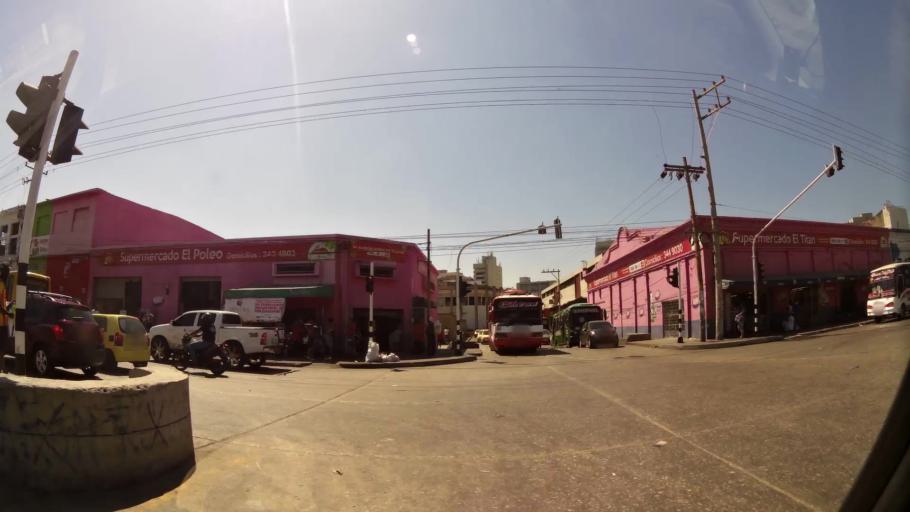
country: CO
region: Atlantico
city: Barranquilla
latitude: 10.9825
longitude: -74.7756
